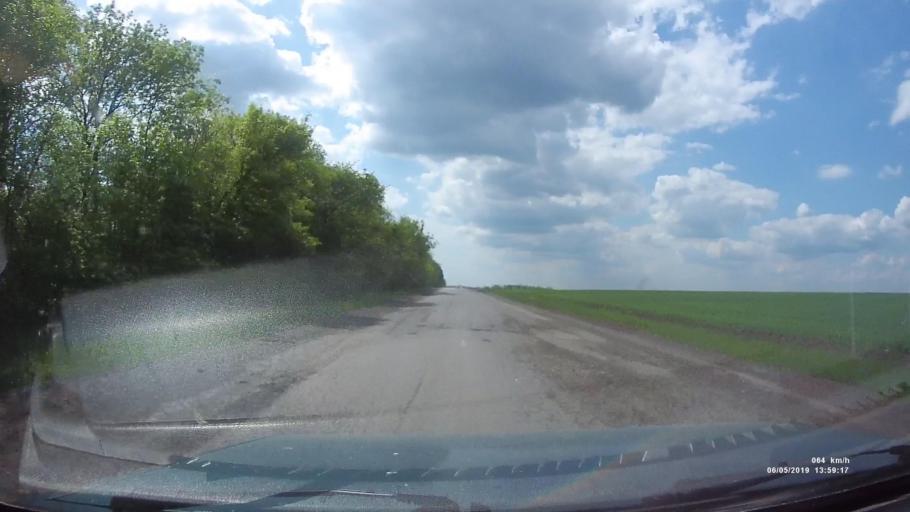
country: RU
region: Rostov
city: Shakhty
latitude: 47.6854
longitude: 40.4014
